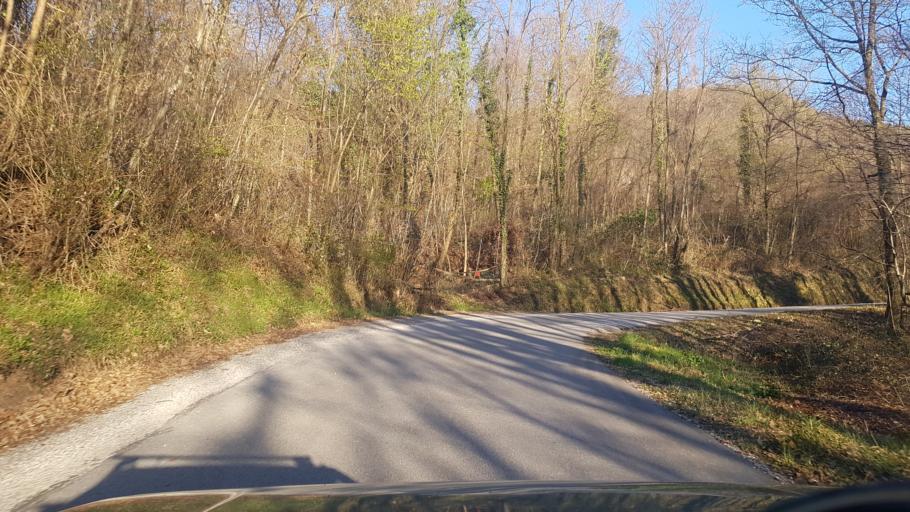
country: SI
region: Kanal
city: Kanal
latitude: 46.0807
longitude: 13.6457
